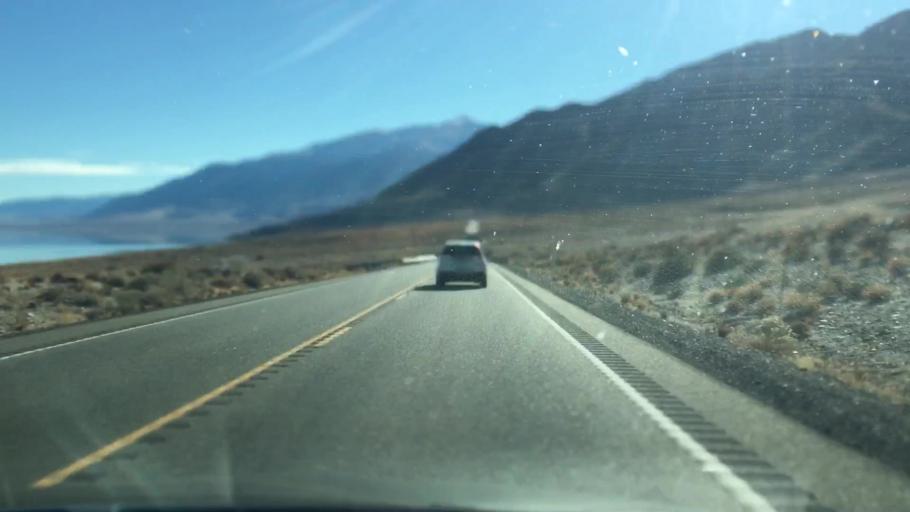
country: US
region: Nevada
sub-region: Mineral County
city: Hawthorne
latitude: 38.7449
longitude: -118.7671
